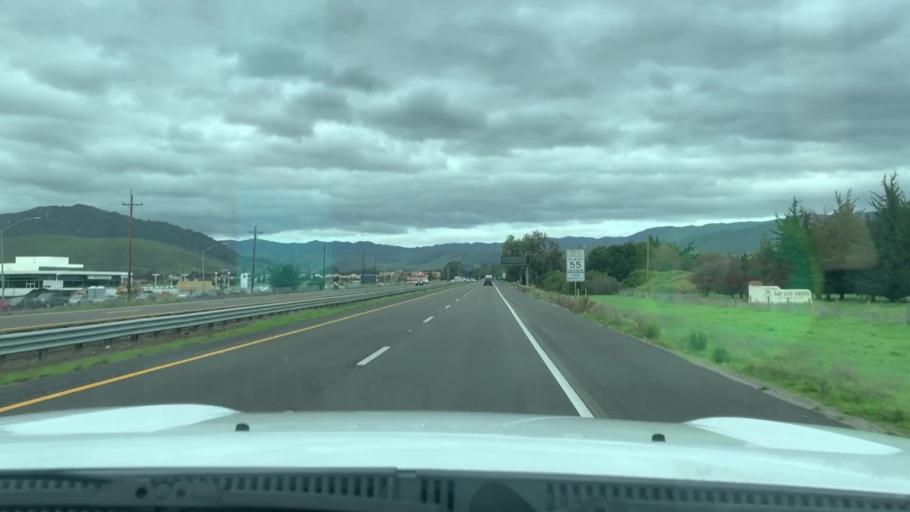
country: US
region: California
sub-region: San Luis Obispo County
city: San Luis Obispo
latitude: 35.2486
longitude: -120.6796
